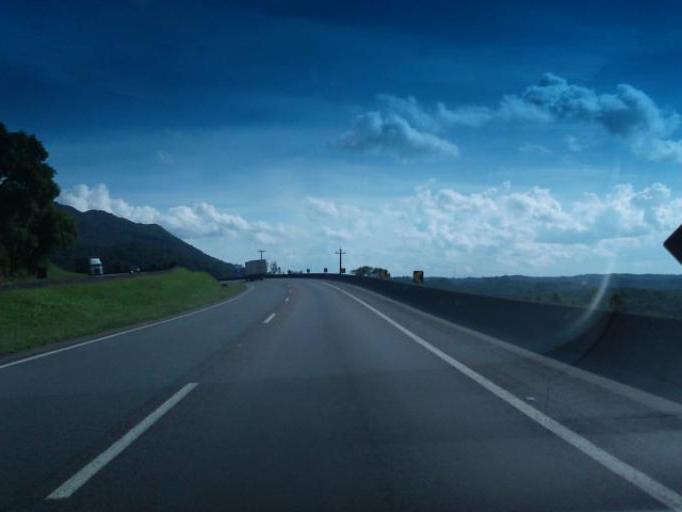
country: BR
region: Parana
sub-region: Campina Grande Do Sul
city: Campina Grande do Sul
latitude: -25.1590
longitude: -48.8620
